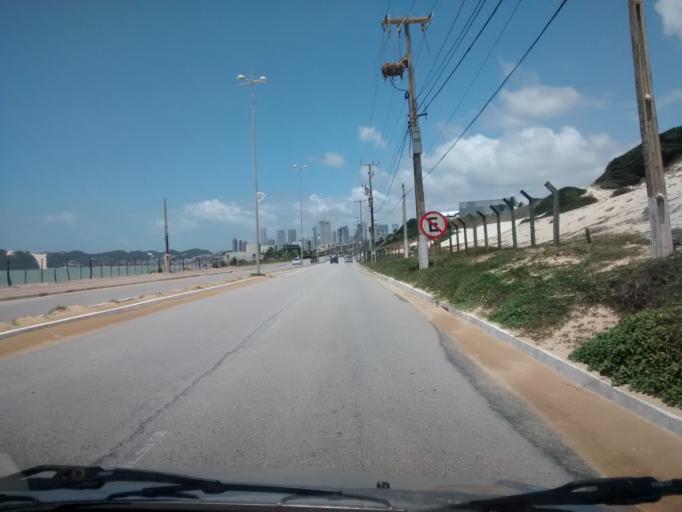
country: BR
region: Rio Grande do Norte
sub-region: Natal
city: Natal
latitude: -5.8573
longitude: -35.1818
